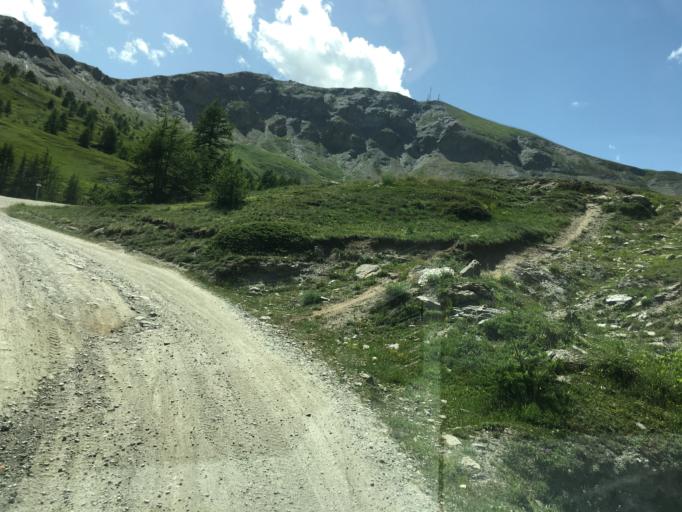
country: IT
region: Piedmont
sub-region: Provincia di Torino
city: Sestriere
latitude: 44.9765
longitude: 6.8785
